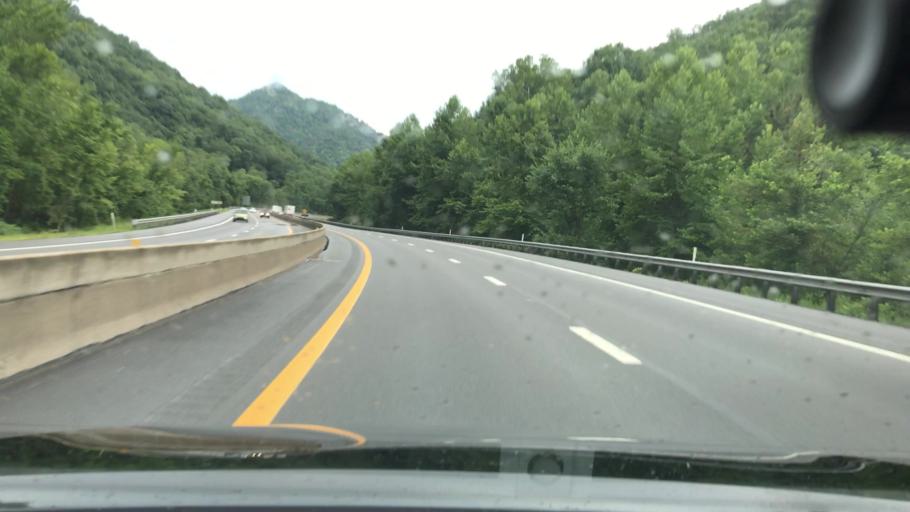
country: US
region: West Virginia
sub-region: Kanawha County
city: Montgomery
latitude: 38.0925
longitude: -81.3909
